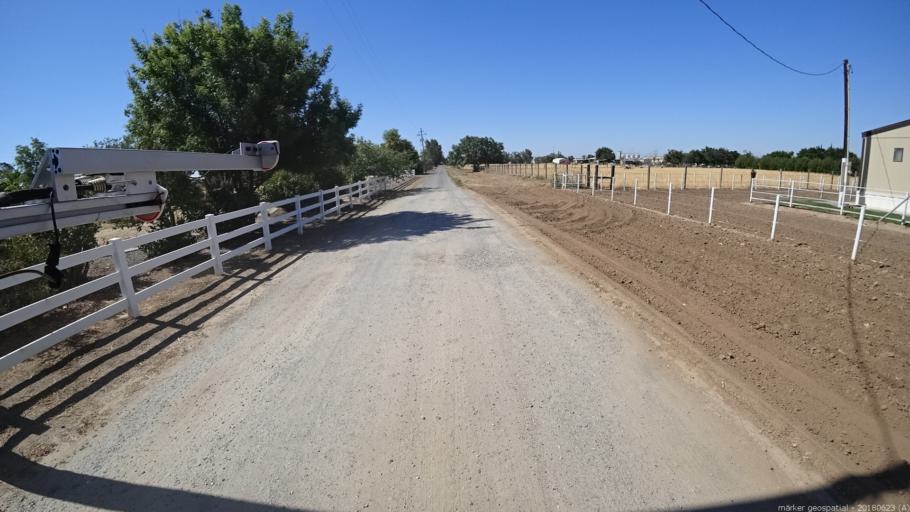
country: US
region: California
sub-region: Madera County
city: Parksdale
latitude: 36.9809
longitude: -120.0173
